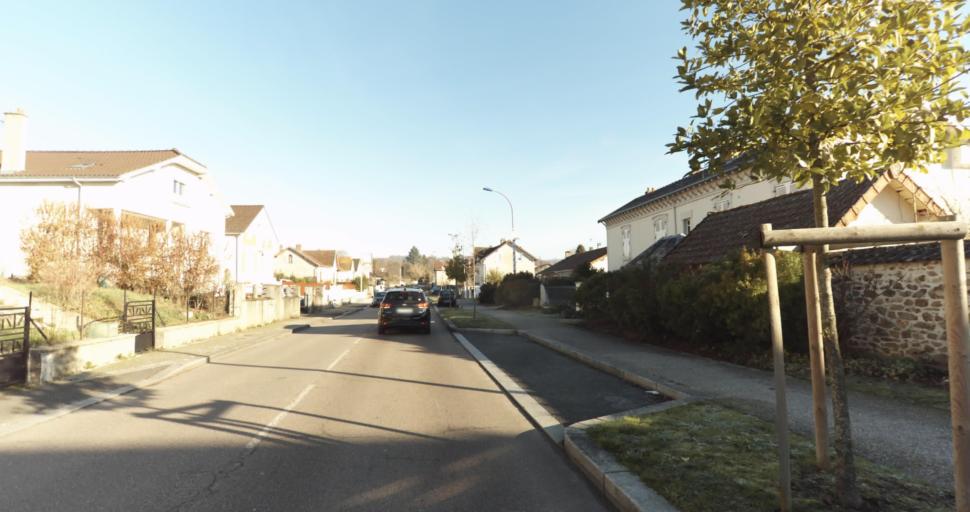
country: FR
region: Limousin
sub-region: Departement de la Haute-Vienne
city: Aixe-sur-Vienne
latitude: 45.8004
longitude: 1.1493
